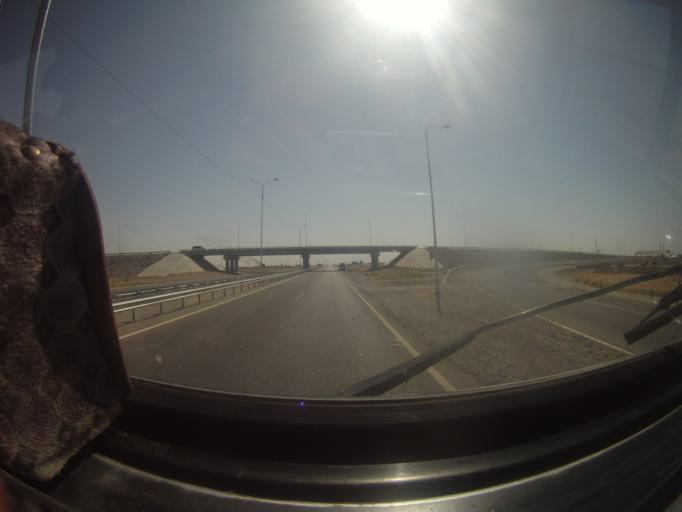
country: KZ
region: Ongtustik Qazaqstan
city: Turkestan
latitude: 43.4142
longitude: 68.0258
